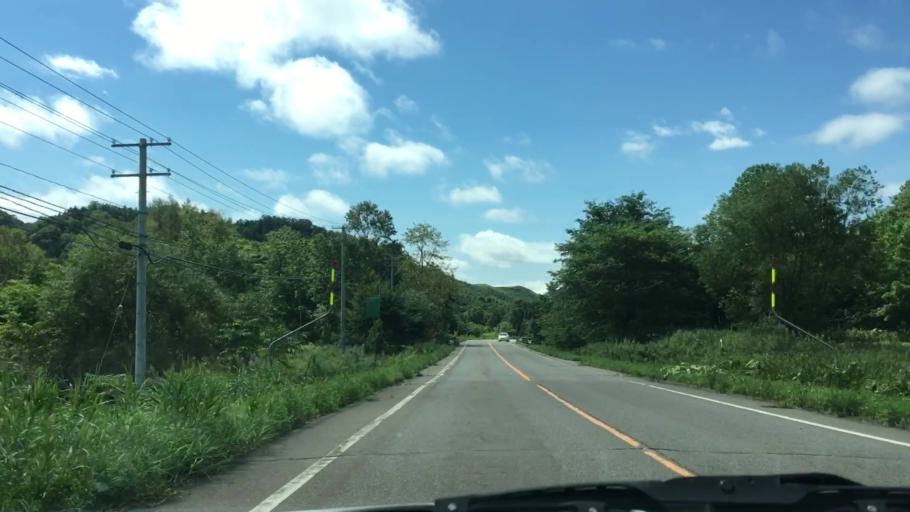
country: JP
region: Hokkaido
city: Kitami
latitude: 43.3412
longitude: 143.7615
